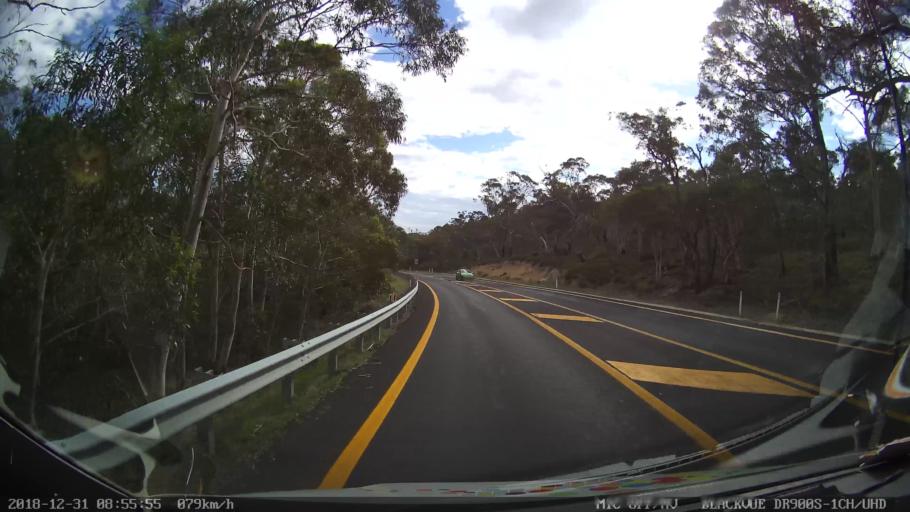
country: AU
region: New South Wales
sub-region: Snowy River
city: Jindabyne
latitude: -36.3445
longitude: 148.5741
